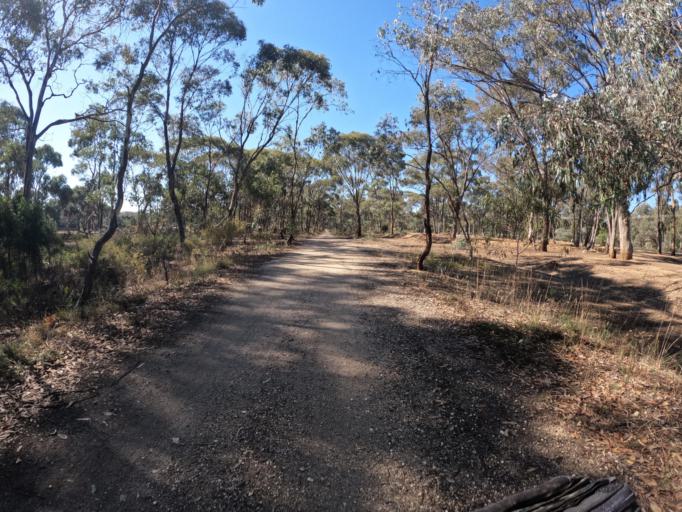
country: AU
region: Victoria
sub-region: Greater Bendigo
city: Kennington
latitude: -36.7762
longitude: 144.3612
